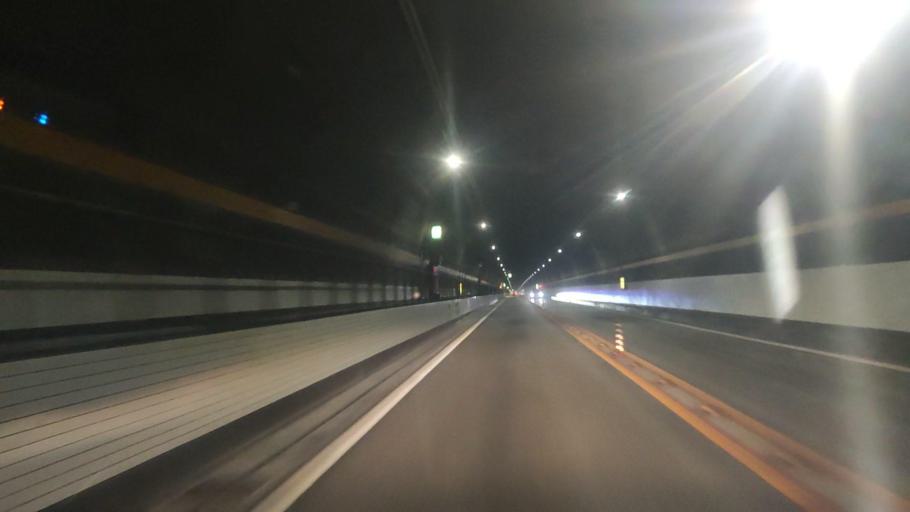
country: JP
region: Nagasaki
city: Obita
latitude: 32.7833
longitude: 129.8844
